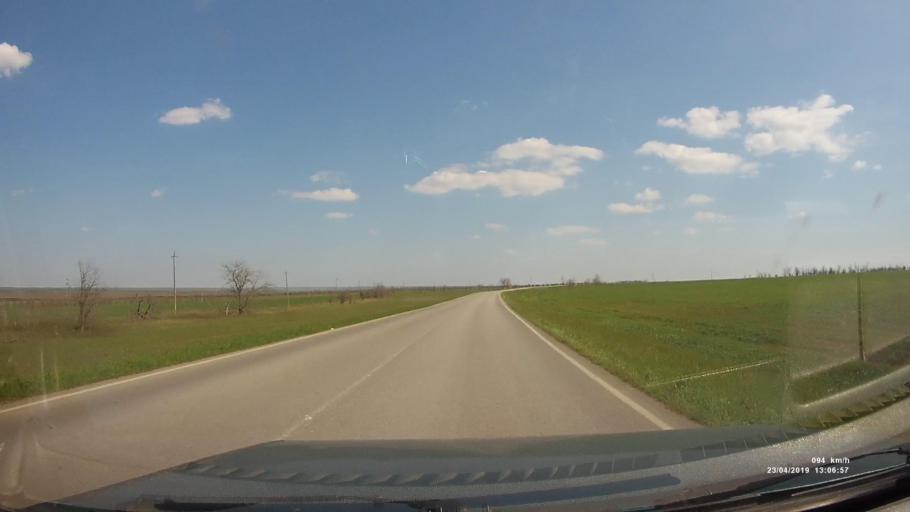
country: RU
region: Kalmykiya
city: Yashalta
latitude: 46.5918
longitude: 42.7516
